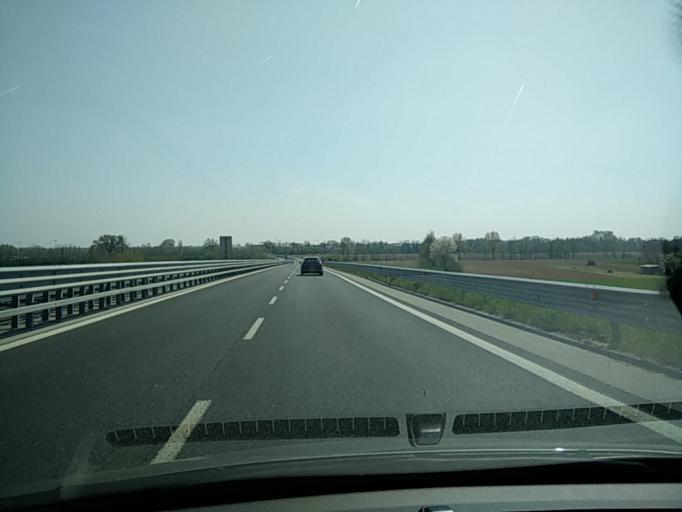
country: IT
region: Veneto
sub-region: Provincia di Treviso
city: Castagnole
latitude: 45.6653
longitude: 12.1948
